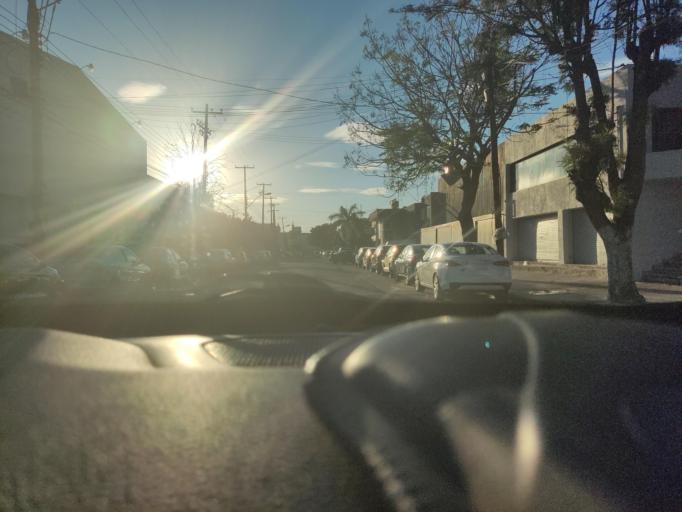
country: MX
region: Guanajuato
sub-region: Leon
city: Medina
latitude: 21.1046
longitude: -101.6325
